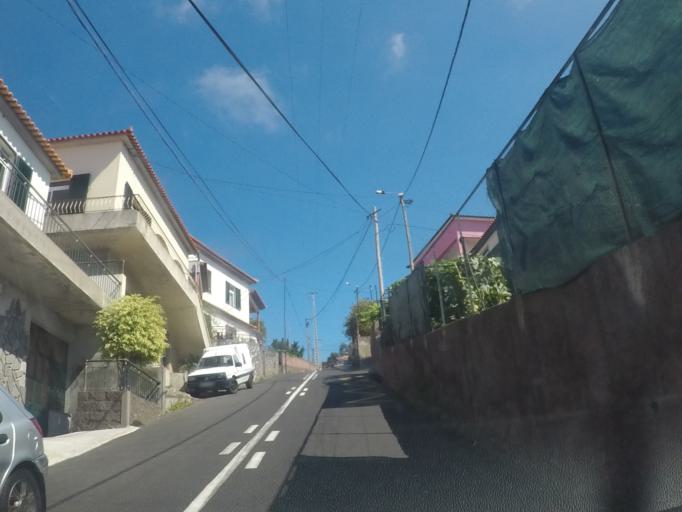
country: PT
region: Madeira
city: Camara de Lobos
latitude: 32.6745
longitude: -16.9647
